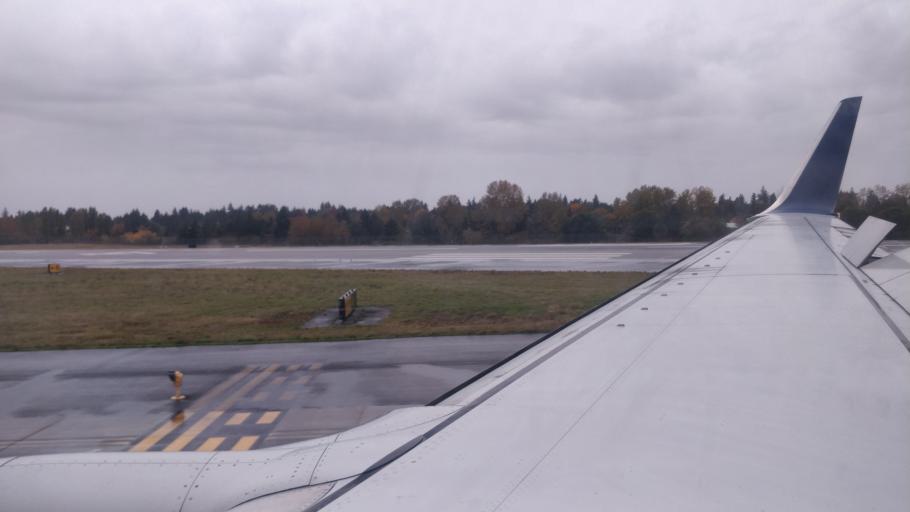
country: US
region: Washington
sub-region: King County
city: Normandy Park
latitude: 47.4424
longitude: -122.3168
